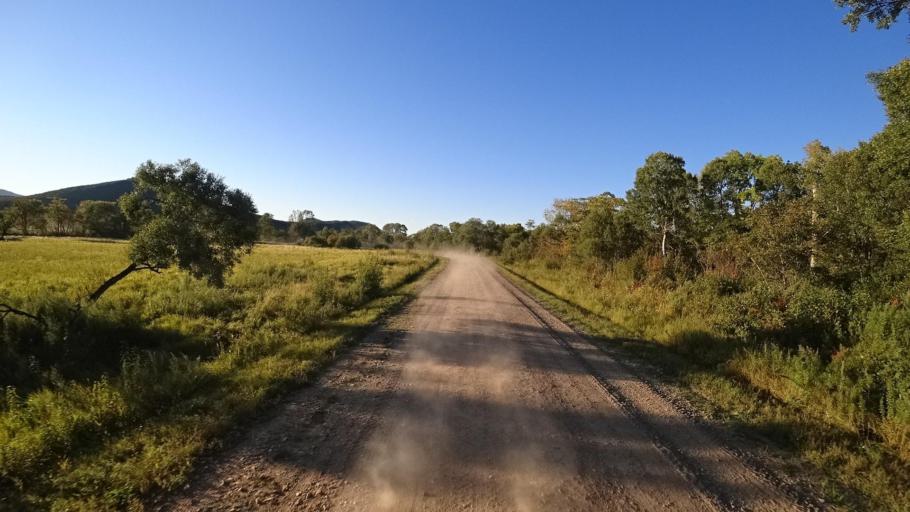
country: RU
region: Primorskiy
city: Kirovskiy
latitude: 44.8318
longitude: 133.5892
